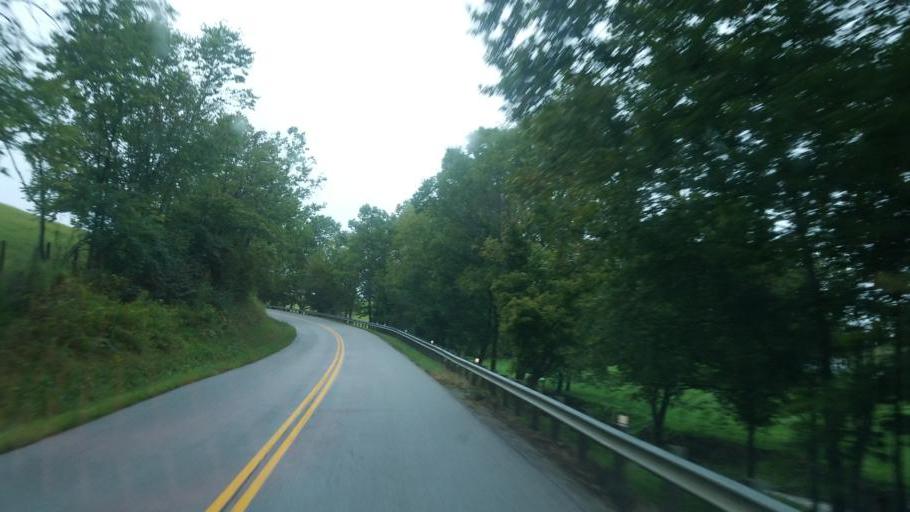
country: US
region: Kentucky
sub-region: Fleming County
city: Flemingsburg
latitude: 38.4264
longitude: -83.7118
